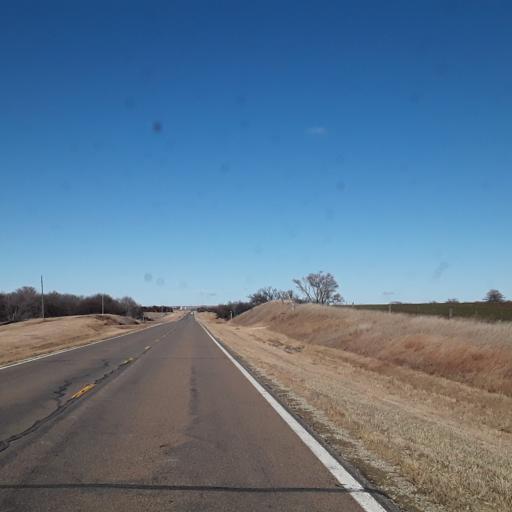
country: US
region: Kansas
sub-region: Lincoln County
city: Lincoln
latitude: 38.9698
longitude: -98.1512
